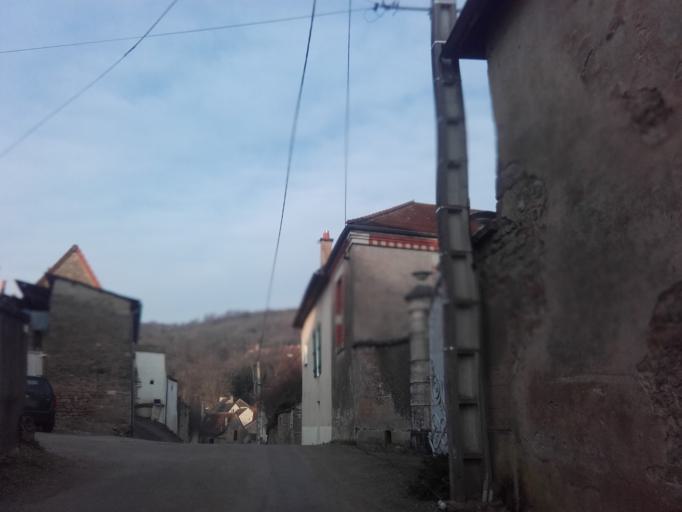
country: FR
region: Bourgogne
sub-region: Departement de la Cote-d'Or
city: Nolay
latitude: 46.9098
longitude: 4.6526
